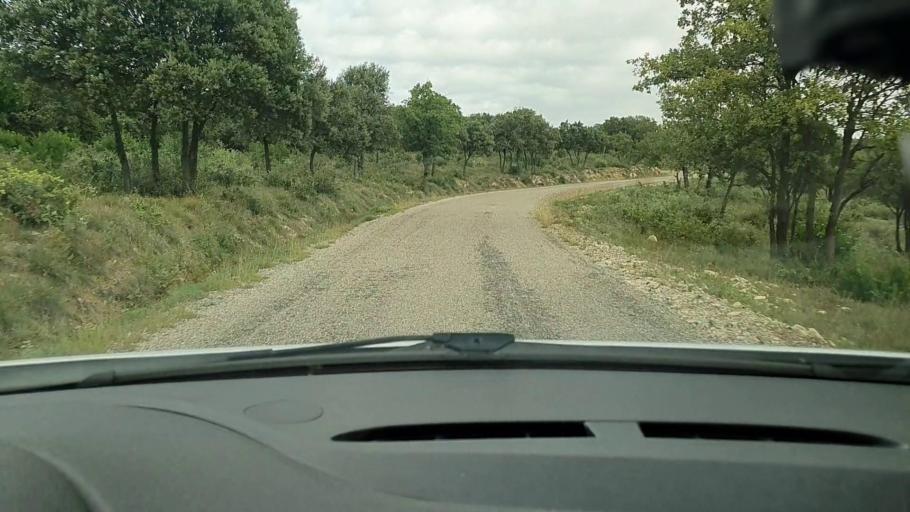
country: FR
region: Languedoc-Roussillon
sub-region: Departement du Gard
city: Montaren-et-Saint-Mediers
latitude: 44.0933
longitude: 4.2959
